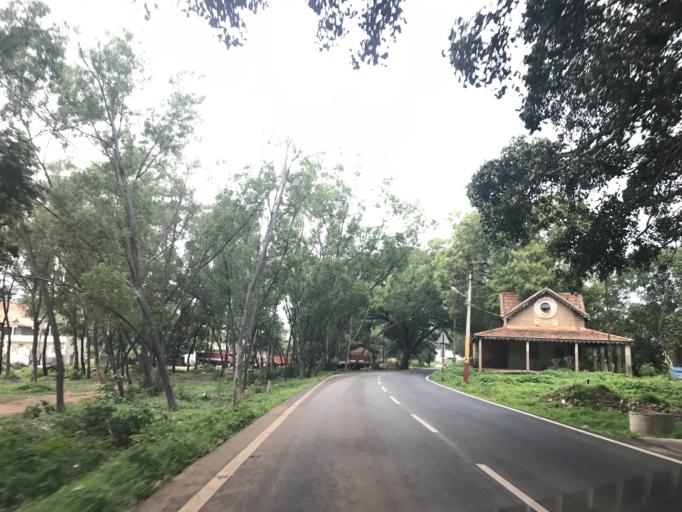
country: IN
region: Karnataka
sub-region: Bangalore Urban
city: Yelahanka
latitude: 13.1803
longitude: 77.6408
